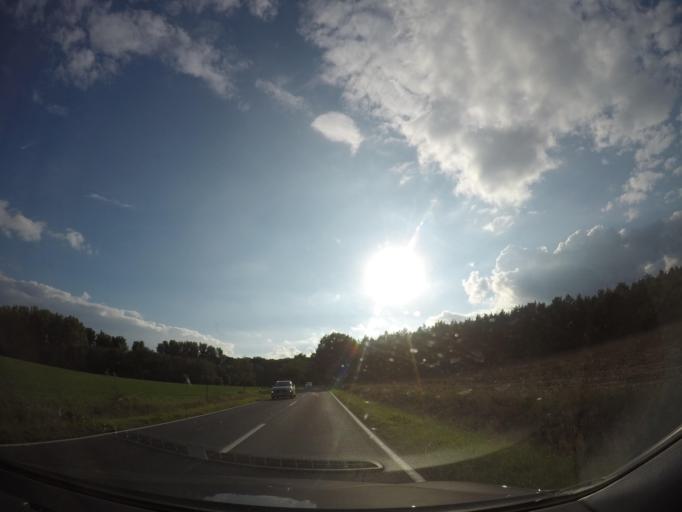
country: DE
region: Saxony-Anhalt
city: Weferlingen
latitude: 52.3652
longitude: 11.0904
